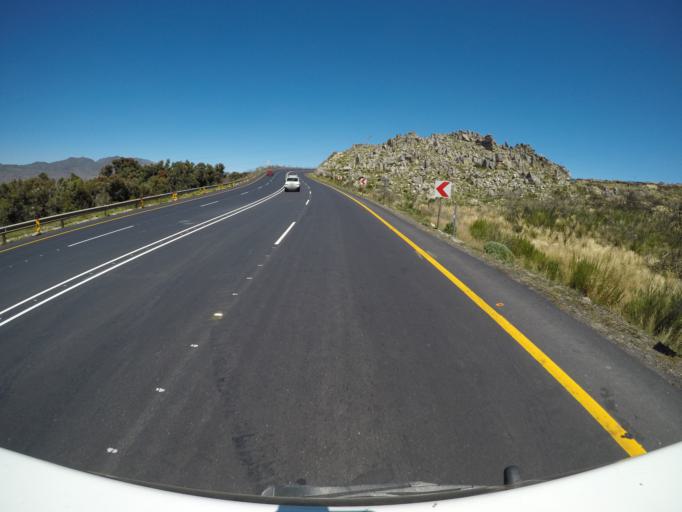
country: ZA
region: Western Cape
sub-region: Overberg District Municipality
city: Grabouw
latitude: -34.1502
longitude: 18.9321
